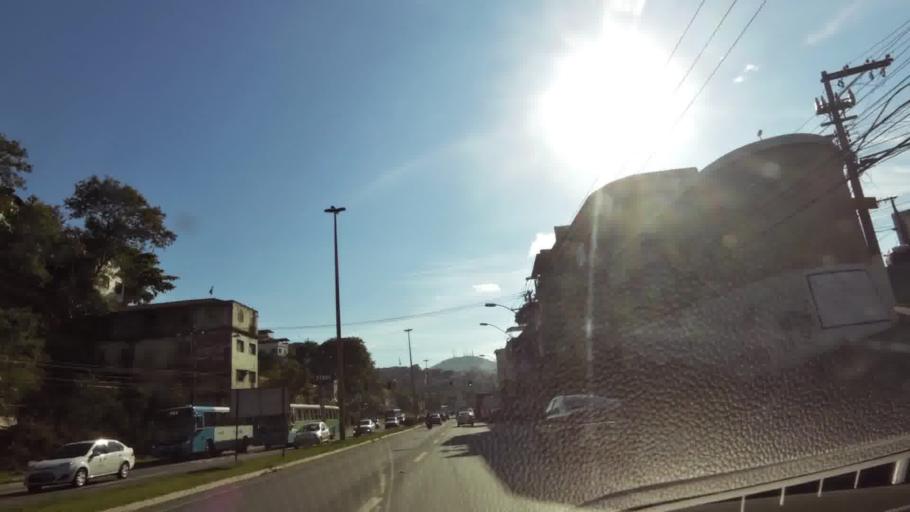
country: BR
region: Espirito Santo
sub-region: Vitoria
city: Vitoria
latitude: -20.3332
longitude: -40.3684
